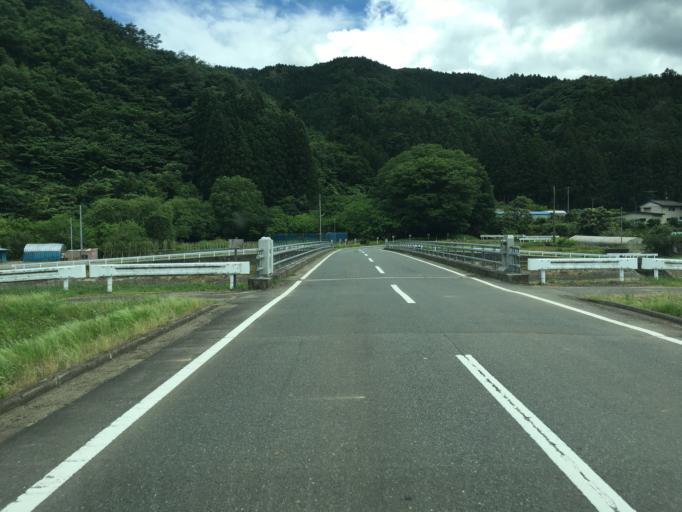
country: JP
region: Miyagi
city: Marumori
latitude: 37.7221
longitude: 140.8888
